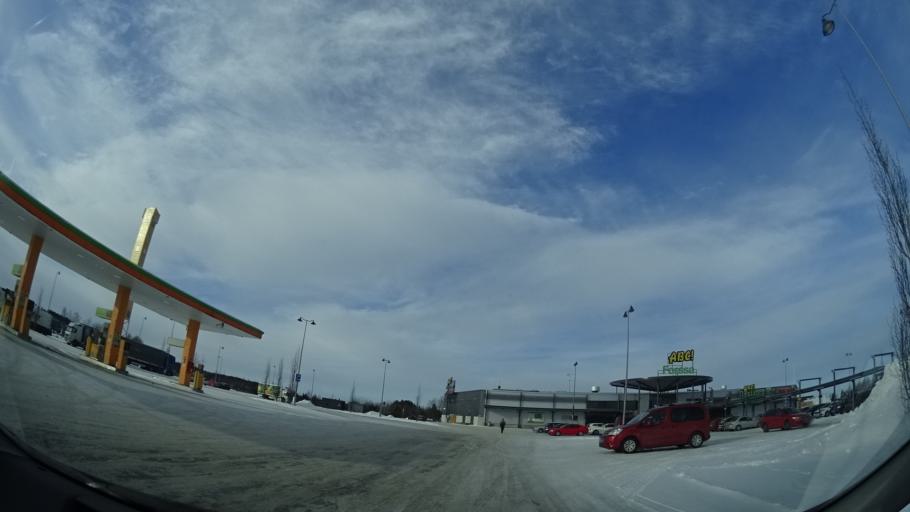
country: FI
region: Haeme
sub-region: Forssa
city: Forssa
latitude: 60.8271
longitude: 23.5731
